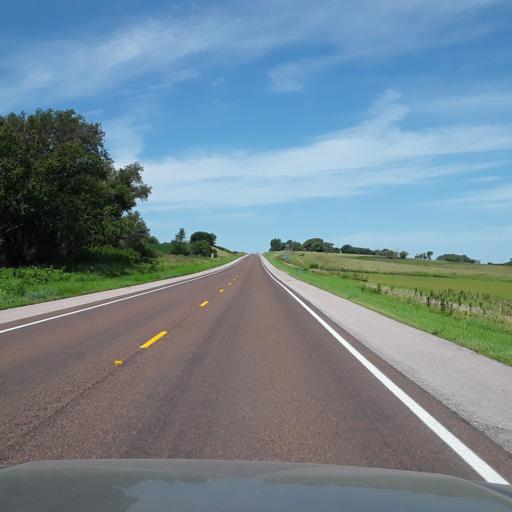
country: US
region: Nebraska
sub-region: Lancaster County
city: Lincoln
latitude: 40.8865
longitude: -96.8383
